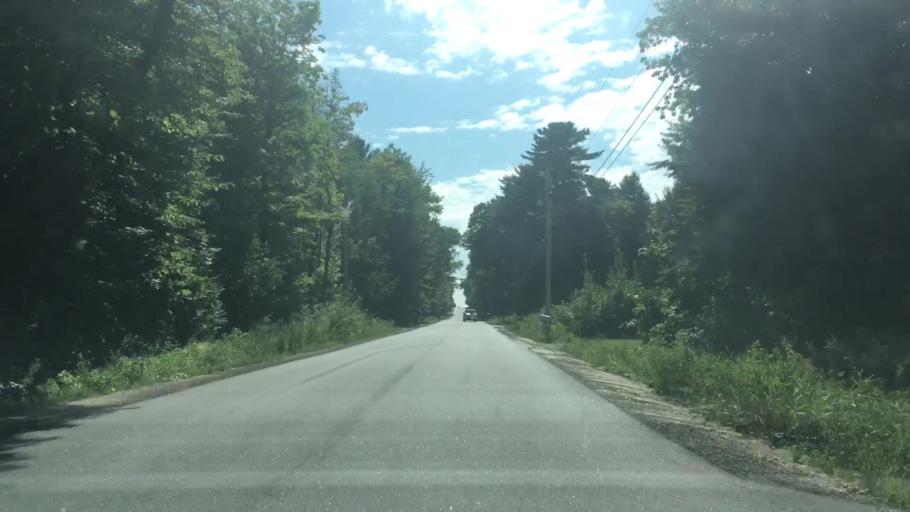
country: US
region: Maine
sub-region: Androscoggin County
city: Poland
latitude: 44.0091
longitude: -70.3672
